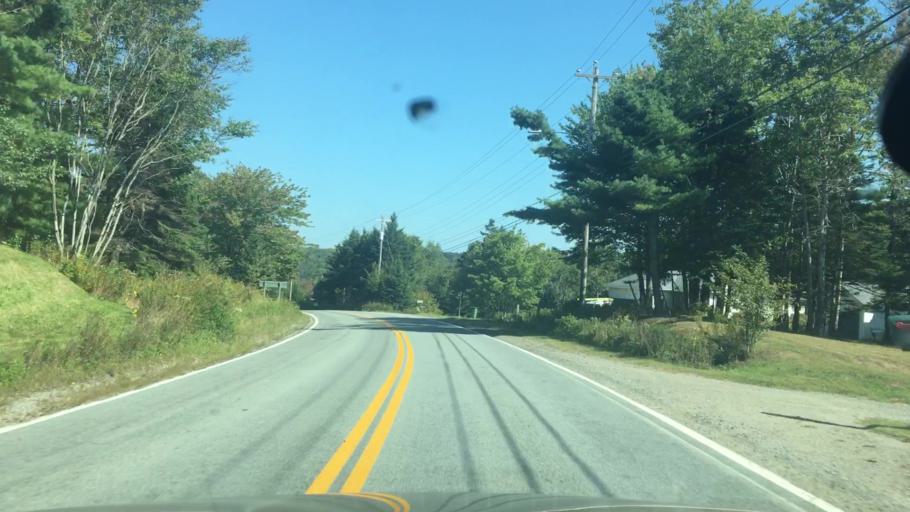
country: CA
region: Nova Scotia
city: New Glasgow
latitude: 44.9141
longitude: -62.5390
